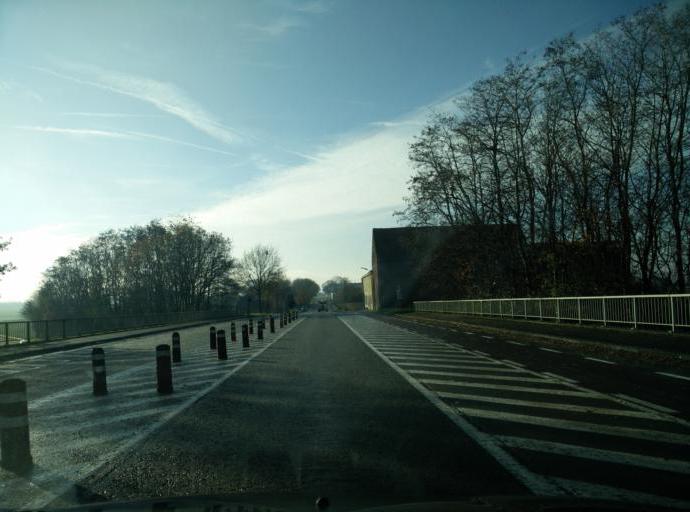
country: BE
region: Wallonia
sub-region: Province du Brabant Wallon
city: Tubize
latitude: 50.7175
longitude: 4.1897
